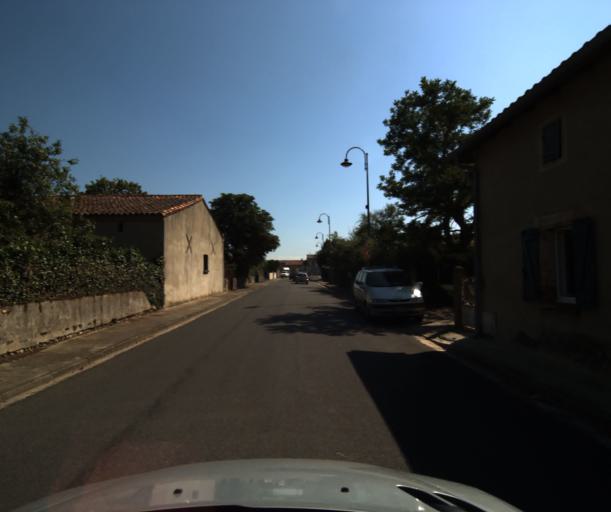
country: FR
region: Midi-Pyrenees
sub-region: Departement de la Haute-Garonne
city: Labarthe-sur-Leze
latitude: 43.4684
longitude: 1.3781
